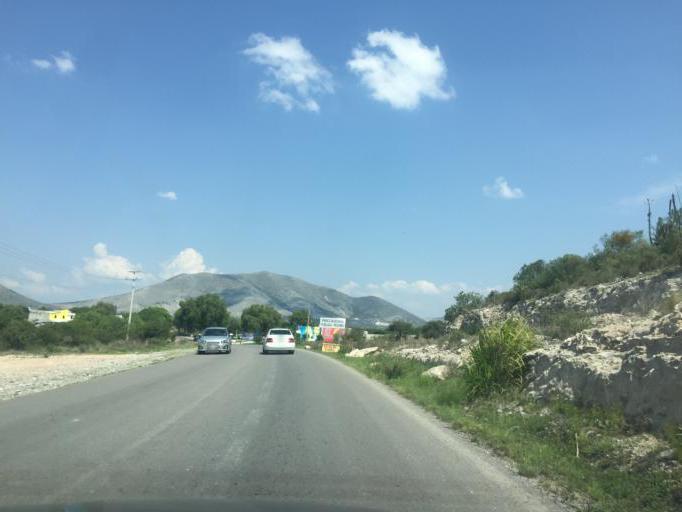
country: MX
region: Hidalgo
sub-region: Cardonal
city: Pozuelos
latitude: 20.6092
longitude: -99.1020
